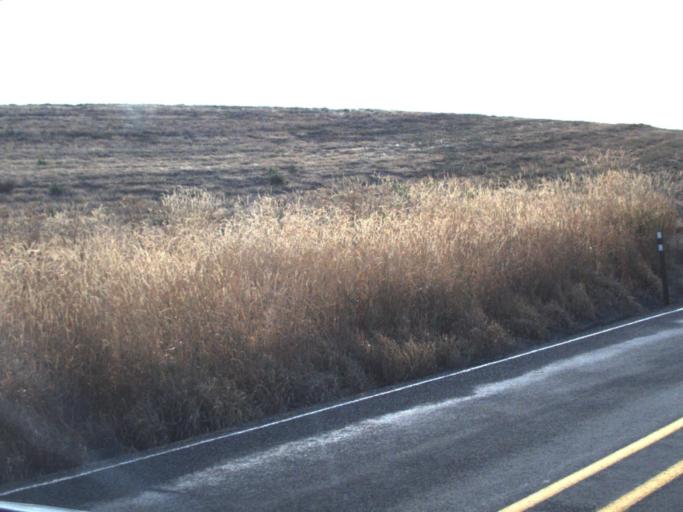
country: US
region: Idaho
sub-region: Benewah County
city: Plummer
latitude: 47.2383
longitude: -117.1196
